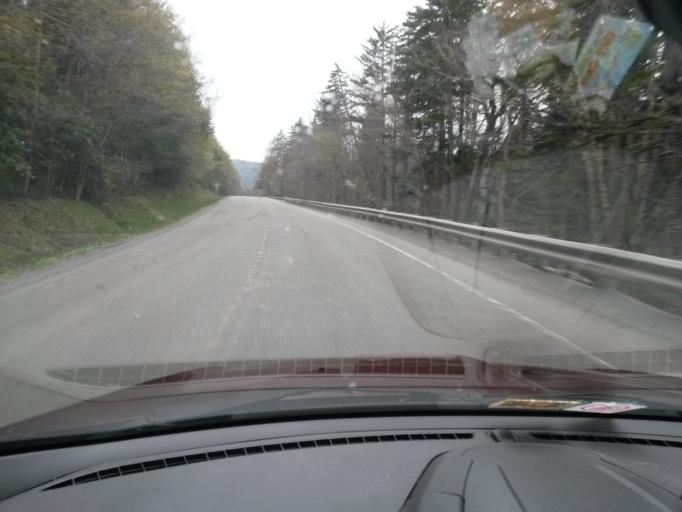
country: US
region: West Virginia
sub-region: Randolph County
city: Elkins
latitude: 38.6301
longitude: -79.8806
